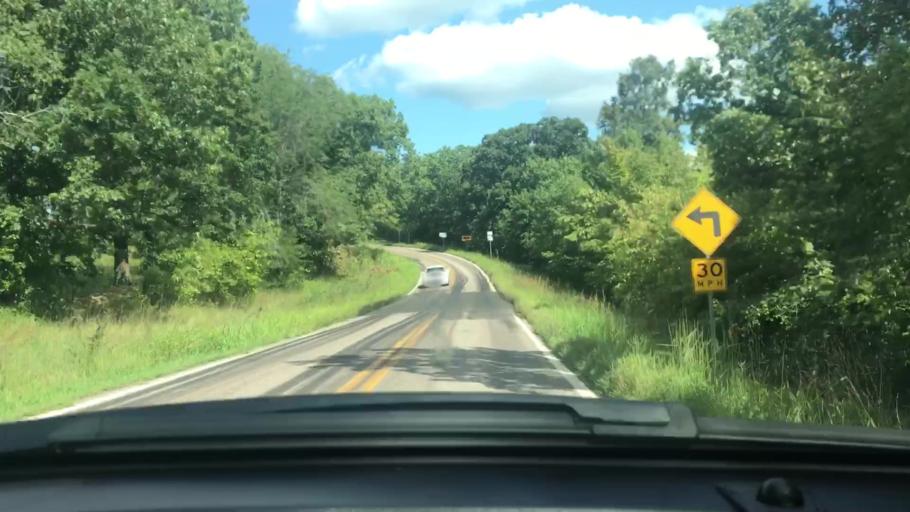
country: US
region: Missouri
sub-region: Wright County
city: Hartville
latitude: 37.3786
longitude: -92.3656
